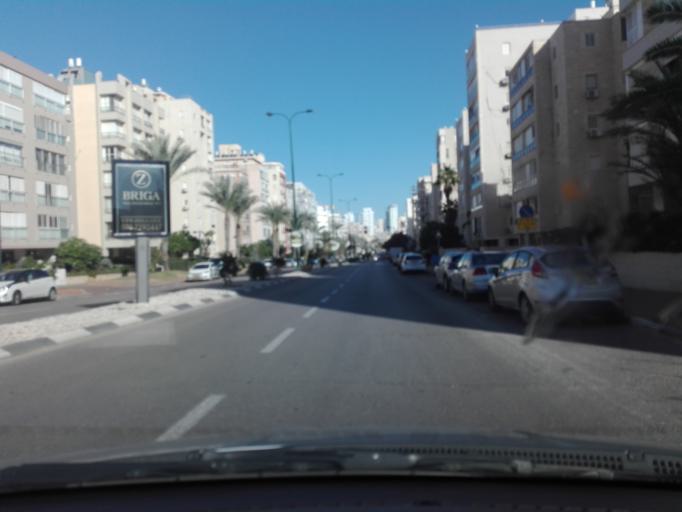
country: IL
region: Central District
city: Netanya
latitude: 32.3200
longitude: 34.8482
